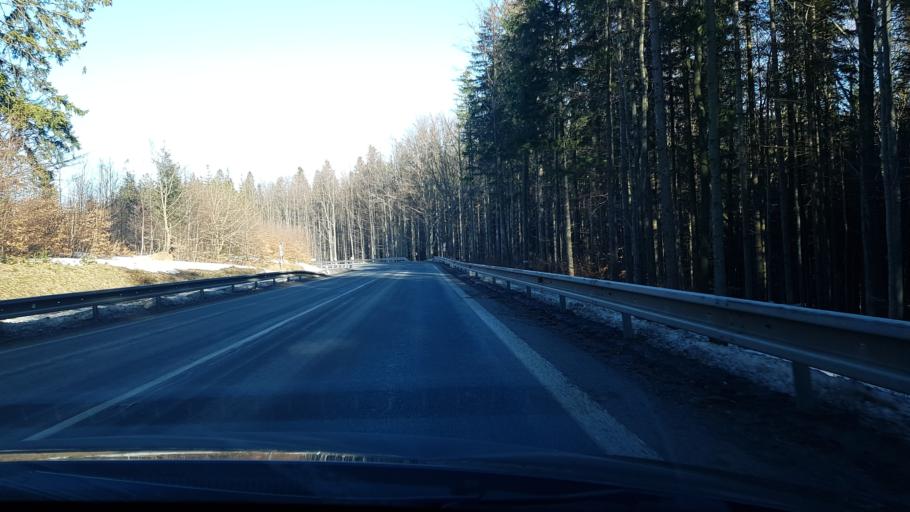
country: CZ
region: Olomoucky
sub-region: Okres Jesenik
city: Jesenik
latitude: 50.1520
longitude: 17.1702
